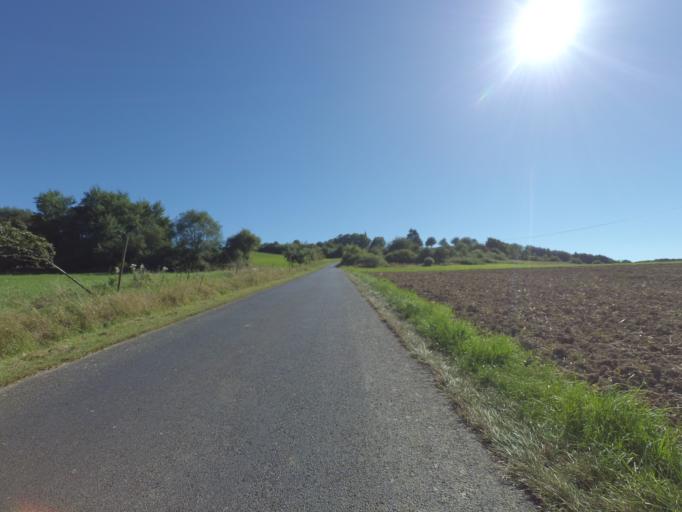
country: DE
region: Rheinland-Pfalz
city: Boxberg
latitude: 50.2588
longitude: 6.8811
